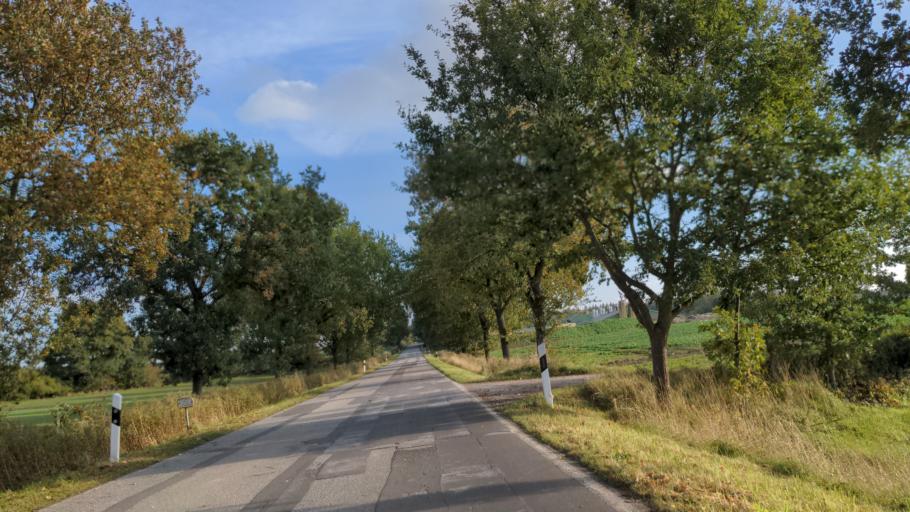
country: DE
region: Schleswig-Holstein
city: Damlos
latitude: 54.2406
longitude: 10.9100
